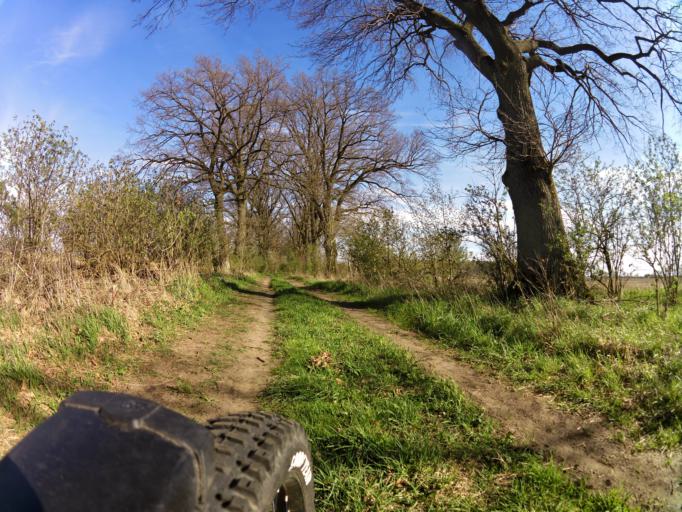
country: PL
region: West Pomeranian Voivodeship
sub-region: Powiat lobeski
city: Resko
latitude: 53.7794
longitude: 15.5551
